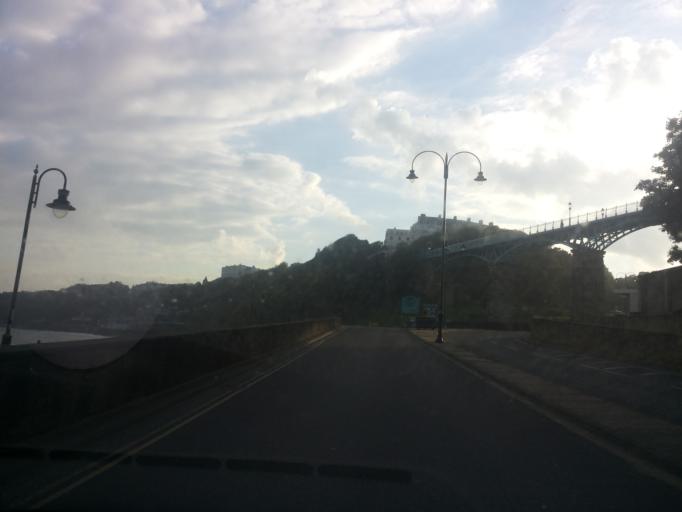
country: GB
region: England
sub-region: North Yorkshire
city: Scarborough
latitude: 54.2801
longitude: -0.3974
